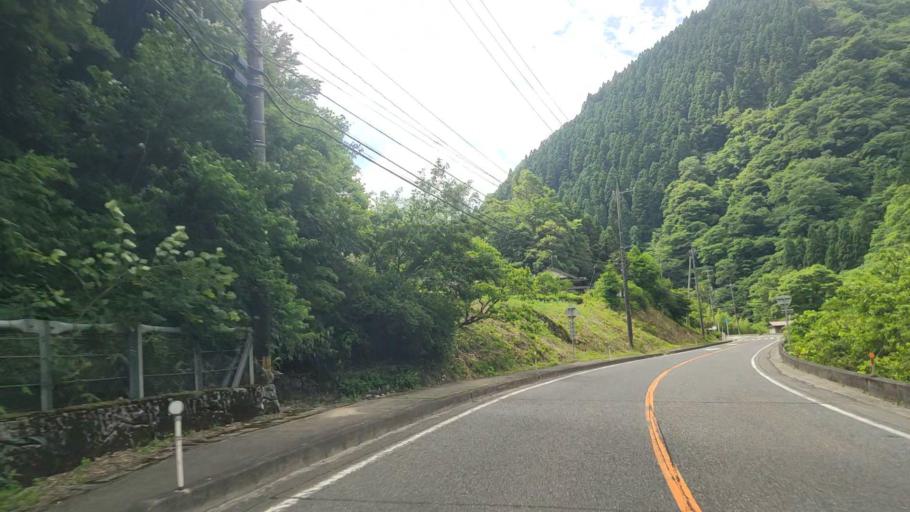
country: JP
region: Tottori
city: Yonago
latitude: 35.2243
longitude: 133.4479
